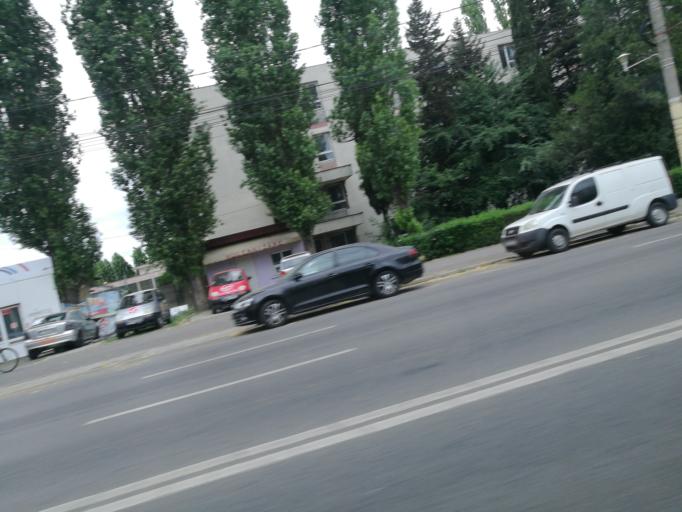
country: RO
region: Constanta
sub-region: Municipiul Constanta
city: Constanta
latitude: 44.1853
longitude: 28.6352
